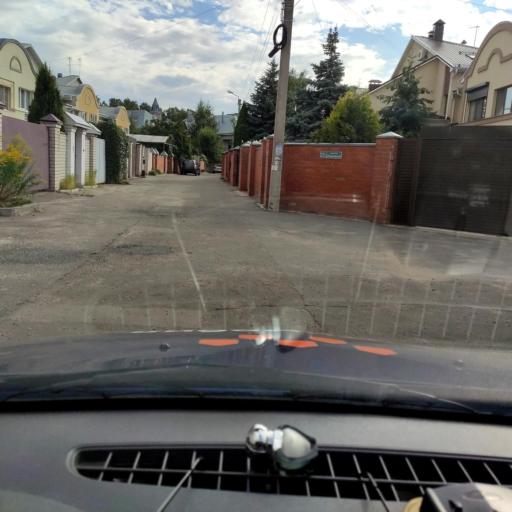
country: RU
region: Voronezj
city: Podgornoye
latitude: 51.7248
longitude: 39.1898
